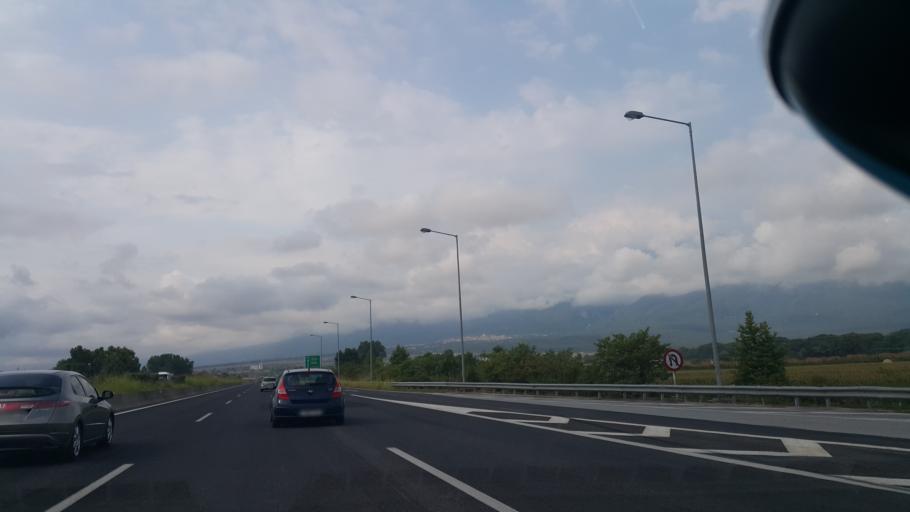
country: GR
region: Central Macedonia
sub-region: Nomos Pierias
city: Dion
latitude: 40.1594
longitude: 22.5439
